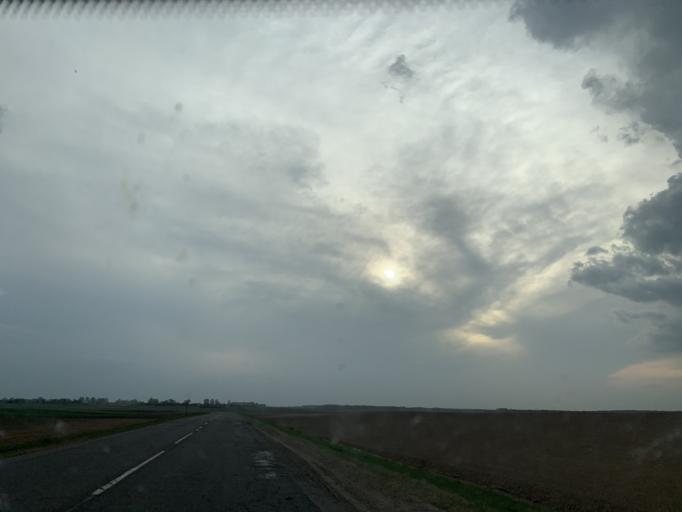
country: BY
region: Minsk
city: Kapyl'
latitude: 53.3014
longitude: 27.0463
